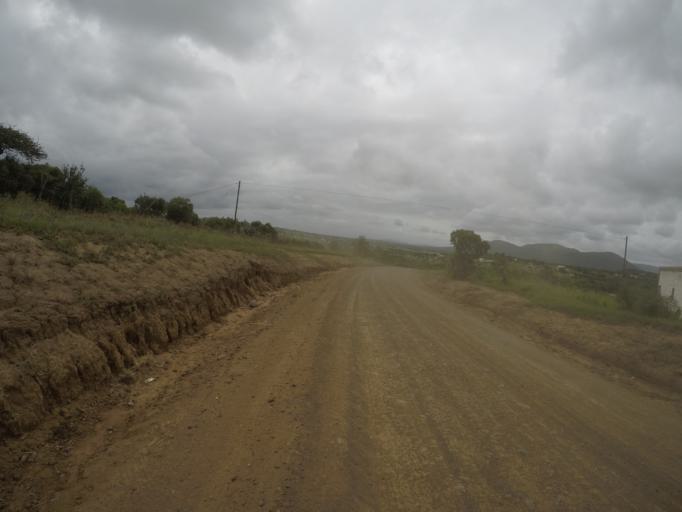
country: ZA
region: KwaZulu-Natal
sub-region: uThungulu District Municipality
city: Empangeni
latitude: -28.5950
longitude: 31.8399
